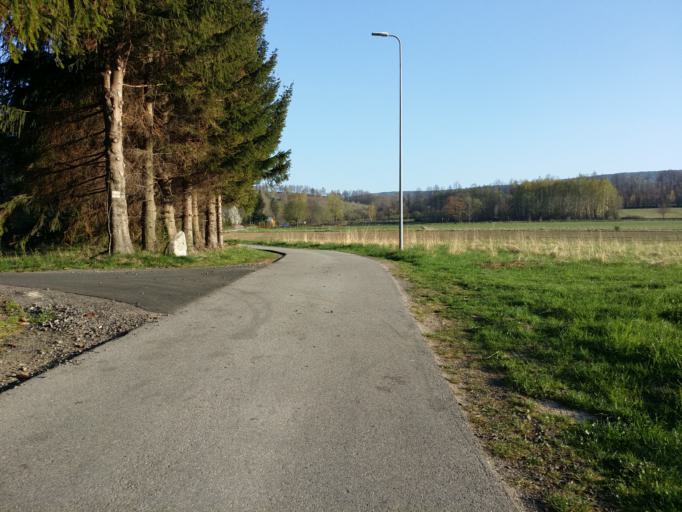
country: PL
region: Lower Silesian Voivodeship
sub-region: Powiat lwowecki
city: Mirsk
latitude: 50.9322
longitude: 15.4372
